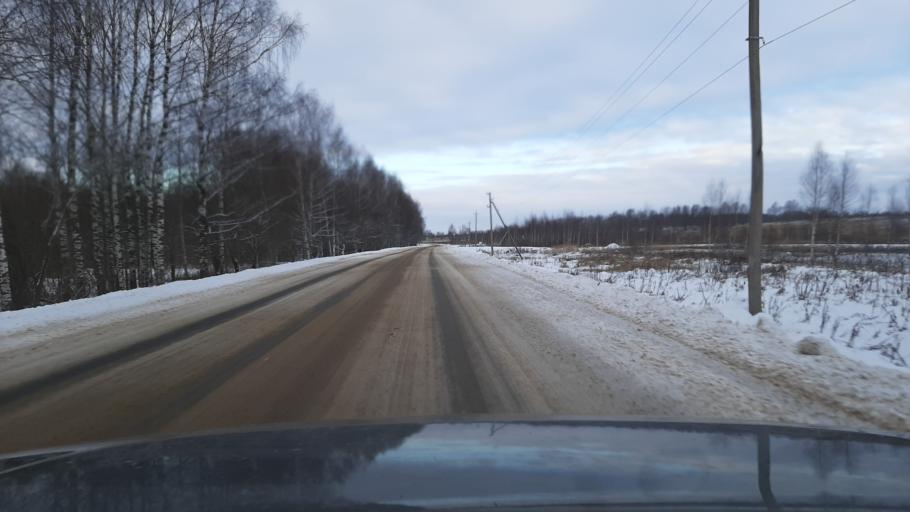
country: RU
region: Kostroma
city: Nerekhta
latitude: 57.4722
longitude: 40.6625
